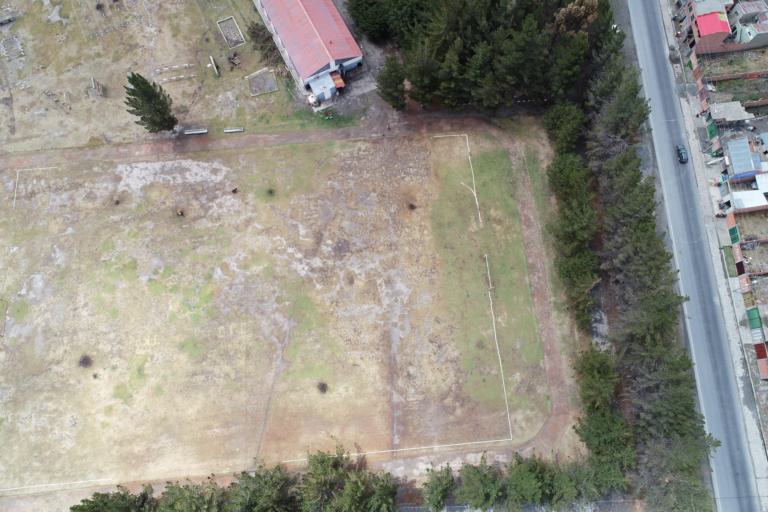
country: BO
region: La Paz
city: Achacachi
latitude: -16.0325
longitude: -68.6879
